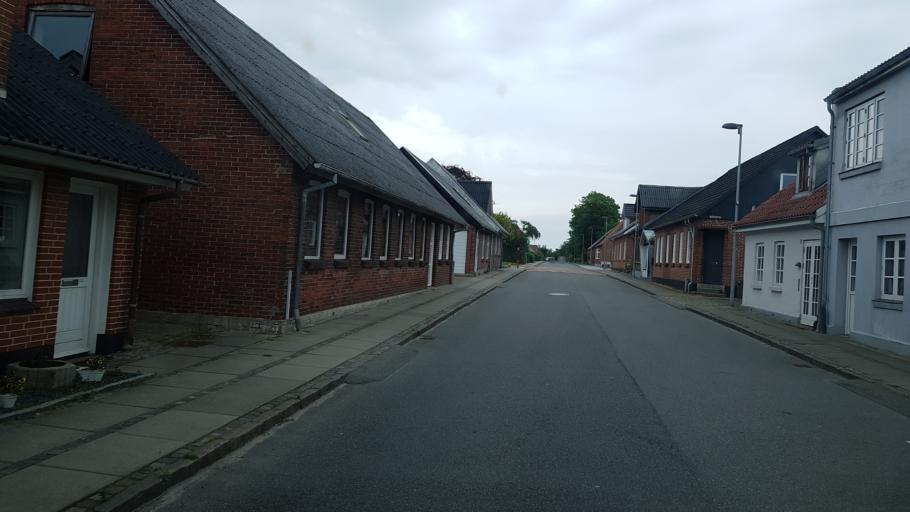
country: DK
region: South Denmark
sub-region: Varde Kommune
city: Olgod
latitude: 55.7165
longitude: 8.6031
